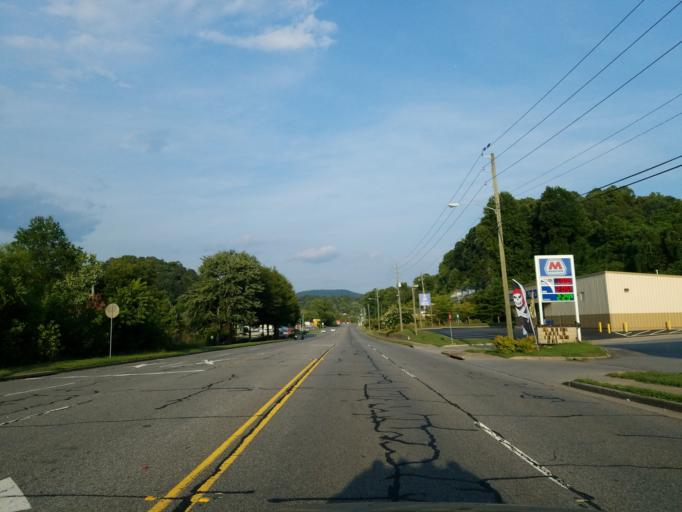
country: US
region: Georgia
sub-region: Gilmer County
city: Ellijay
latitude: 34.6858
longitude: -84.4829
